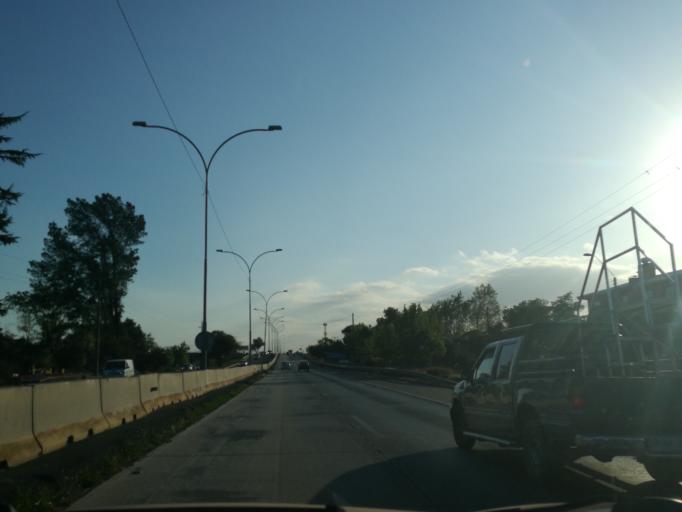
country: CL
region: O'Higgins
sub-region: Provincia de Cachapoal
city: Rancagua
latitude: -34.1769
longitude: -70.7304
